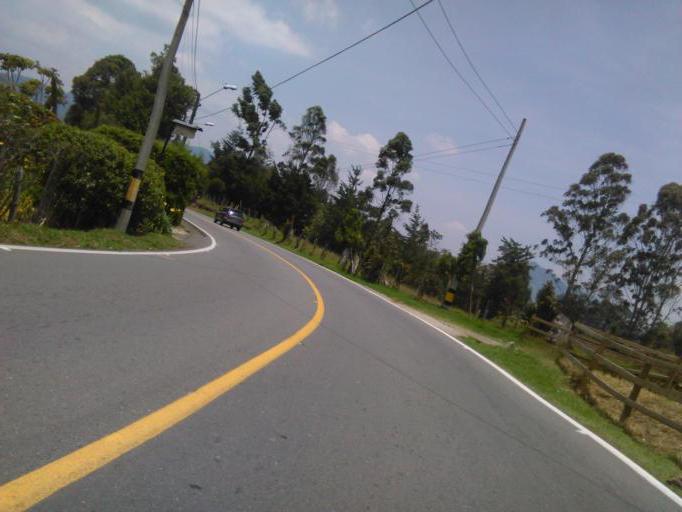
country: CO
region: Antioquia
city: La Ceja
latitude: 6.0145
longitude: -75.4046
